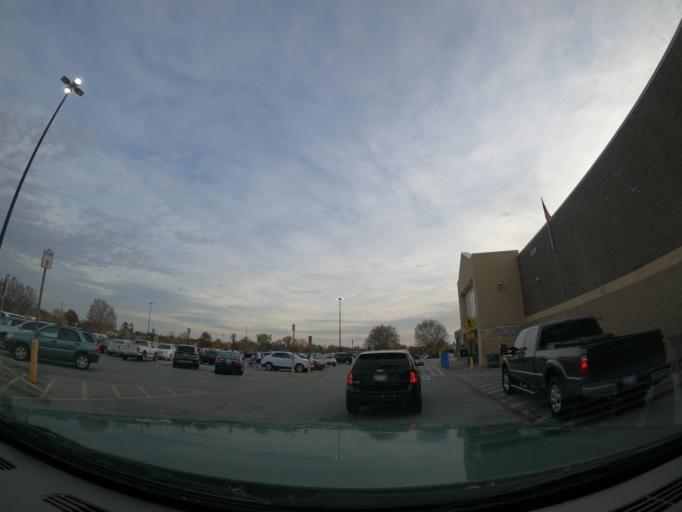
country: US
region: Oklahoma
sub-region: Tulsa County
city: Broken Arrow
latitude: 35.9915
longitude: -95.7999
